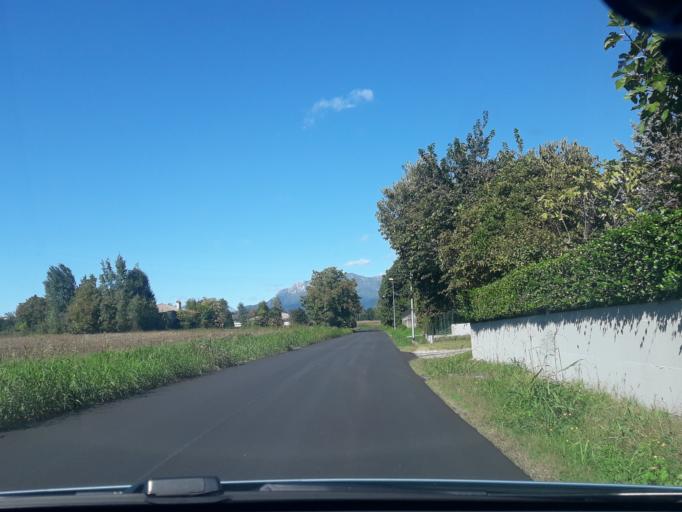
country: IT
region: Friuli Venezia Giulia
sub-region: Provincia di Udine
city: Reana del Roiale
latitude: 46.1406
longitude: 13.2156
